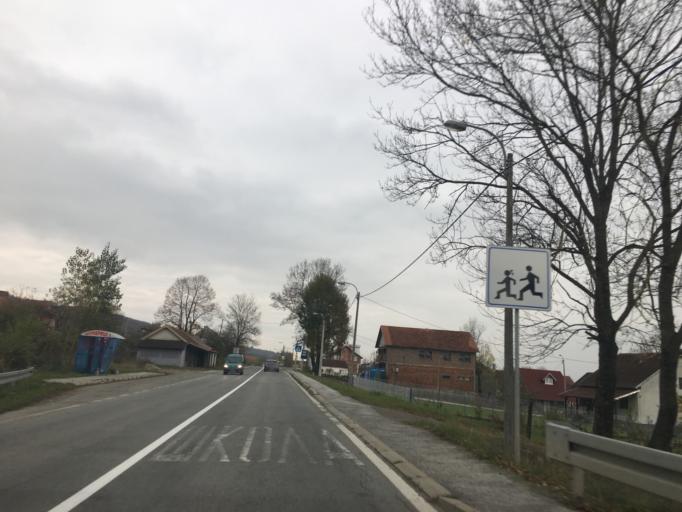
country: RS
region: Central Serbia
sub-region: Raski Okrug
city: Kraljevo
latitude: 43.7269
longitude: 20.7582
